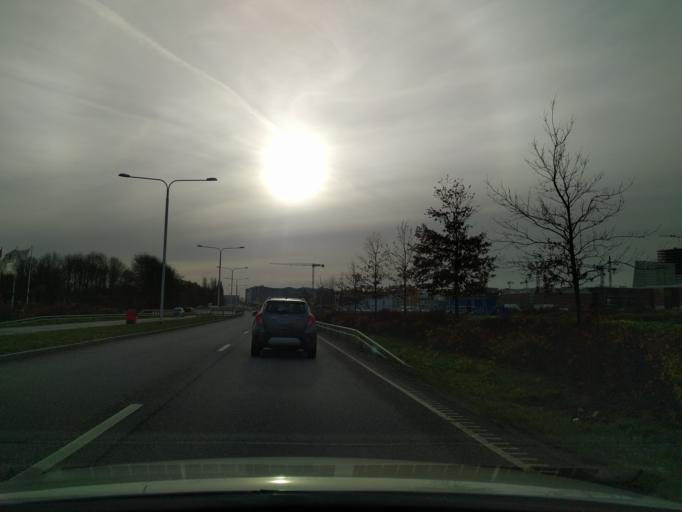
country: SE
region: Skane
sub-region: Malmo
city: Malmoe
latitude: 55.5660
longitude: 12.9855
